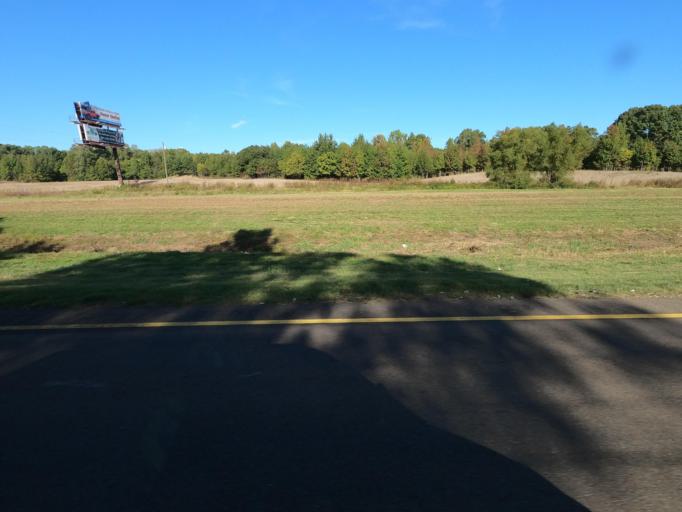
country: US
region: Tennessee
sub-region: Tipton County
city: Atoka
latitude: 35.4591
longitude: -89.7694
